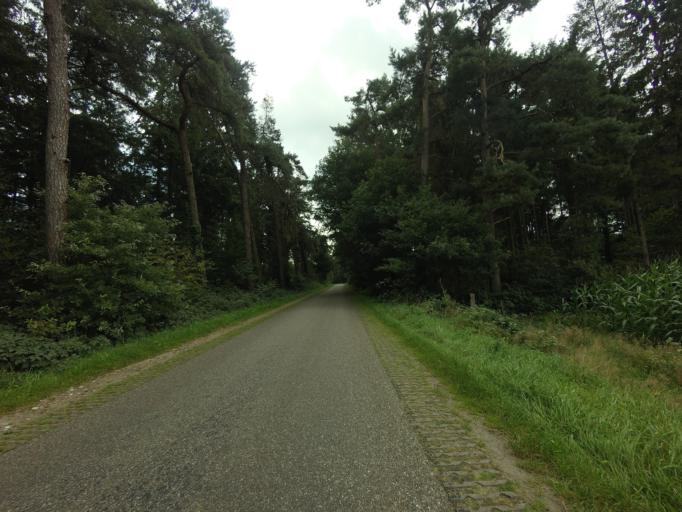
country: NL
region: Overijssel
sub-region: Gemeente Losser
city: Losser
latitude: 52.3467
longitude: 7.0277
